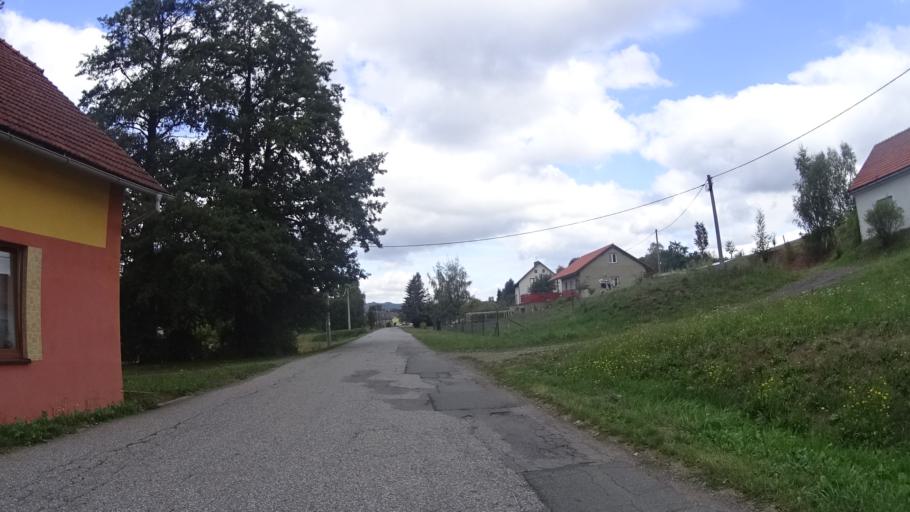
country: CZ
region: Pardubicky
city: Dolni Cermna
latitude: 49.9269
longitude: 16.5460
